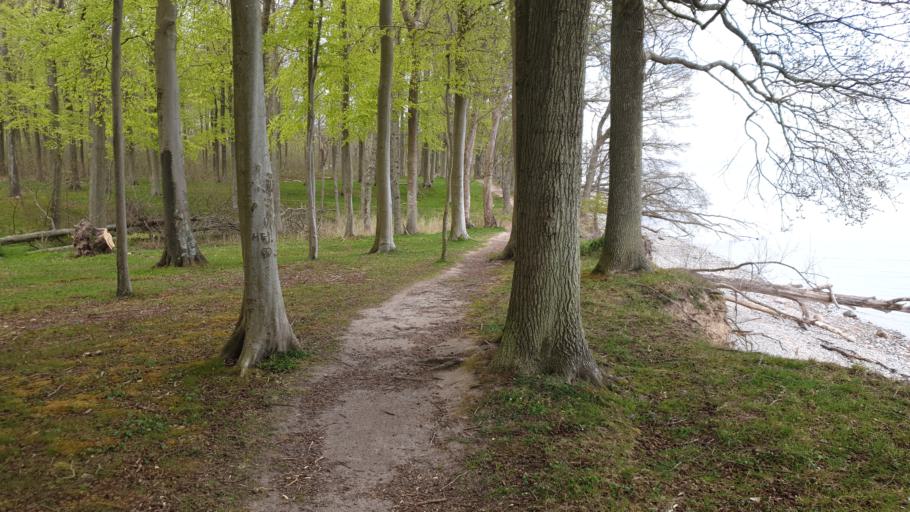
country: DK
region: South Denmark
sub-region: Sonderborg Kommune
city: Dybbol
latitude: 54.8552
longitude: 9.7586
